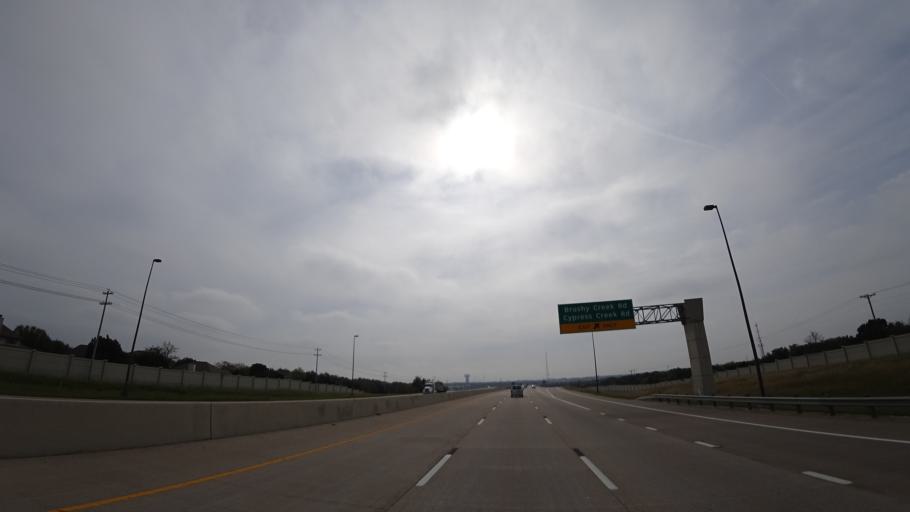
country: US
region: Texas
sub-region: Williamson County
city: Cedar Park
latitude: 30.5080
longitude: -97.8108
